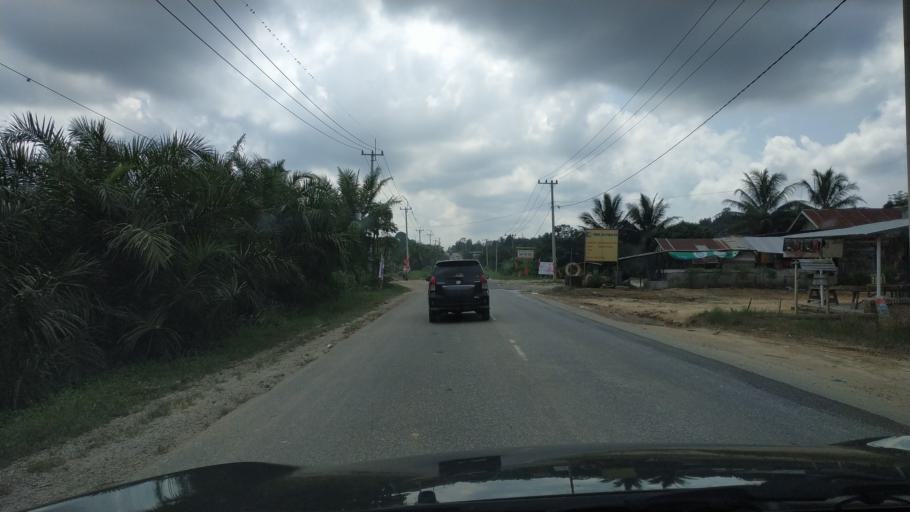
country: ID
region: Riau
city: Pangkalanbunut
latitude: 0.3047
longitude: 101.9100
